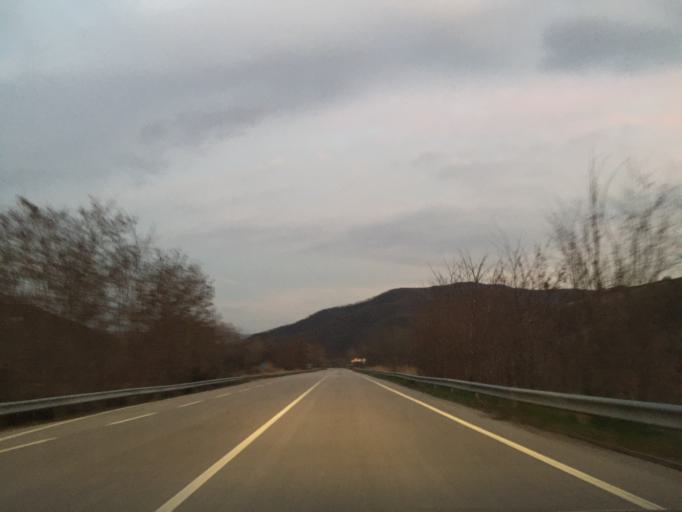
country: IT
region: Apulia
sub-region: Provincia di Foggia
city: San Marco la Catola
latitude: 41.5055
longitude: 14.9986
